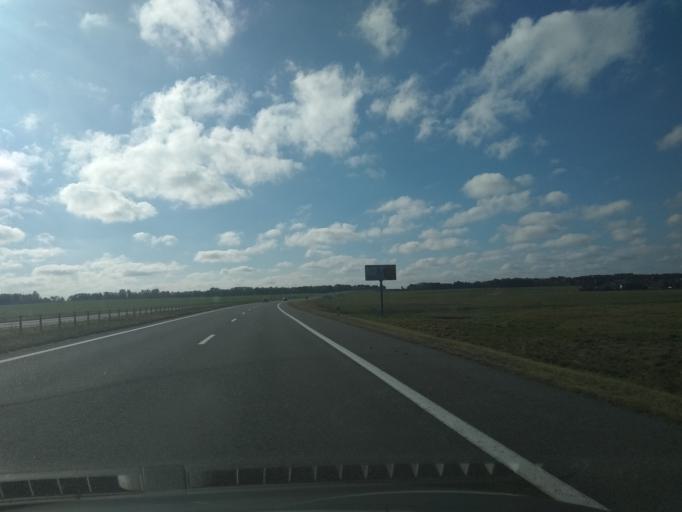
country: BY
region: Minsk
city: Stan'kava
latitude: 53.6931
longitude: 27.2096
